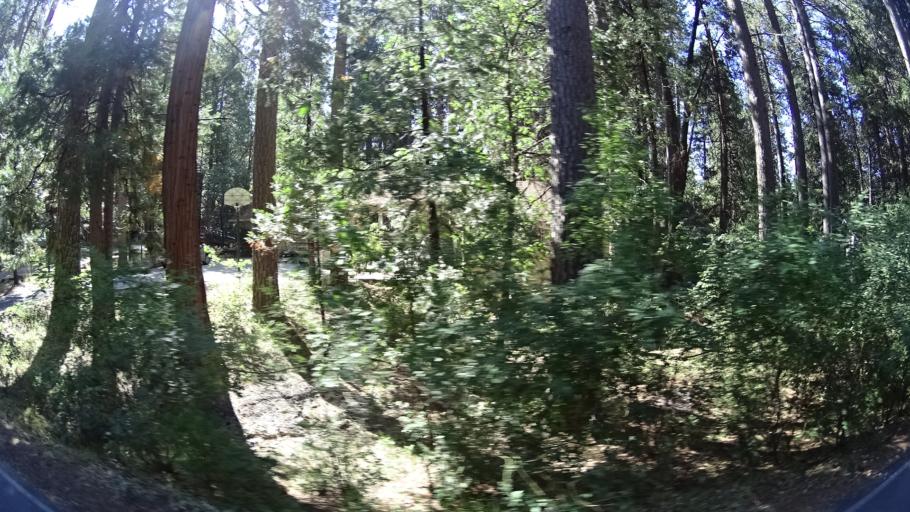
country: US
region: California
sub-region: Calaveras County
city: Arnold
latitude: 38.2402
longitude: -120.3660
